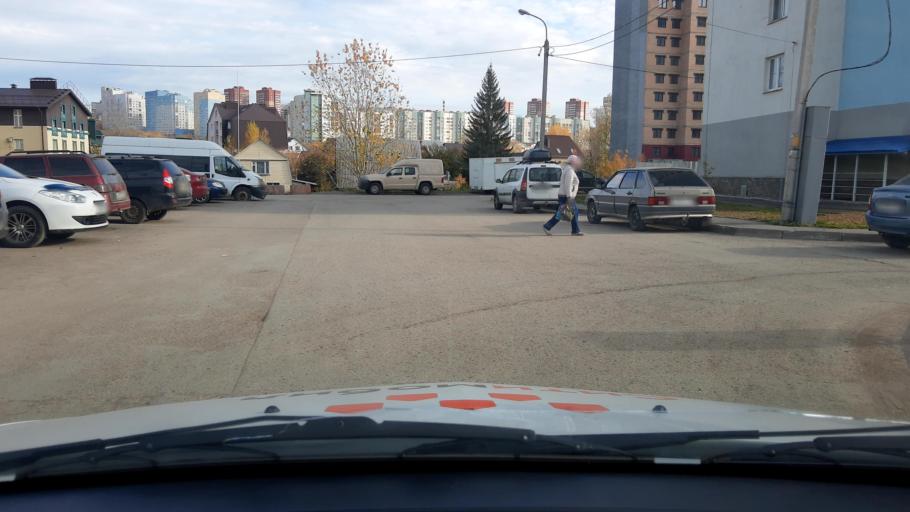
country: RU
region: Bashkortostan
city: Ufa
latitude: 54.6859
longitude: 55.9831
